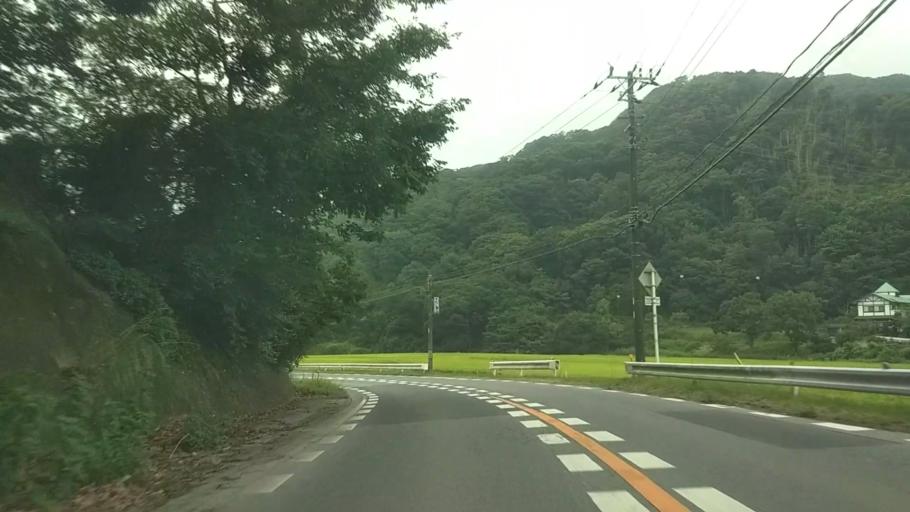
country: JP
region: Chiba
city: Tateyama
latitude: 35.1446
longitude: 139.8715
